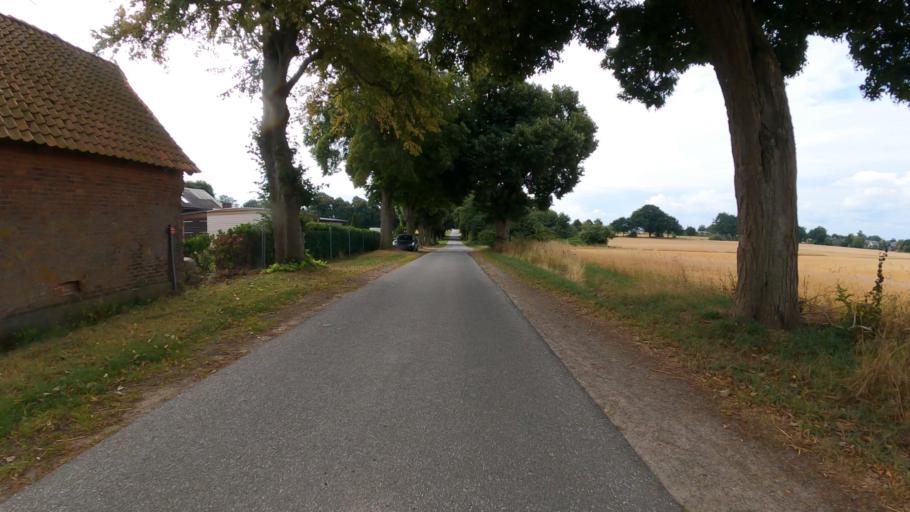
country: DE
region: Lower Saxony
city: Neu Wulmstorf
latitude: 53.4290
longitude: 9.8020
